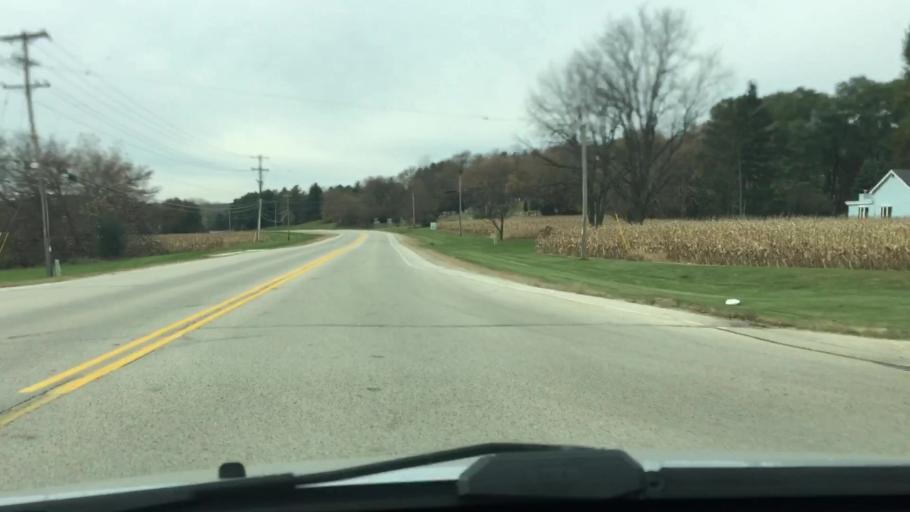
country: US
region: Wisconsin
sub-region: Waukesha County
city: Big Bend
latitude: 42.9029
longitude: -88.2583
